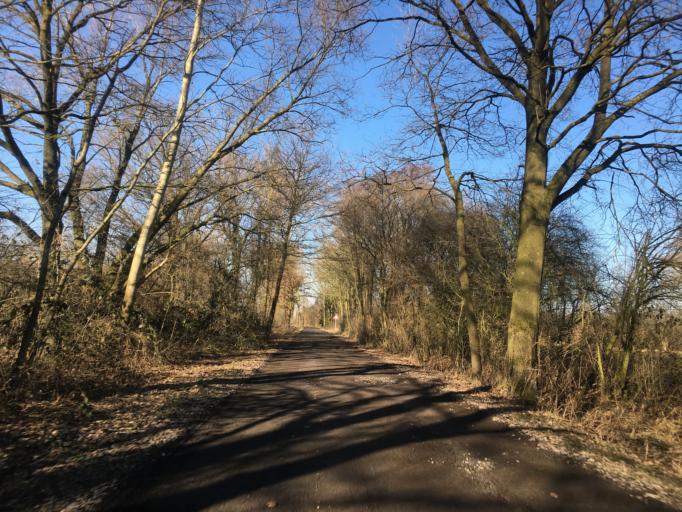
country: DE
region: North Rhine-Westphalia
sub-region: Regierungsbezirk Munster
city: Altenberge
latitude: 52.0050
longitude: 7.5162
